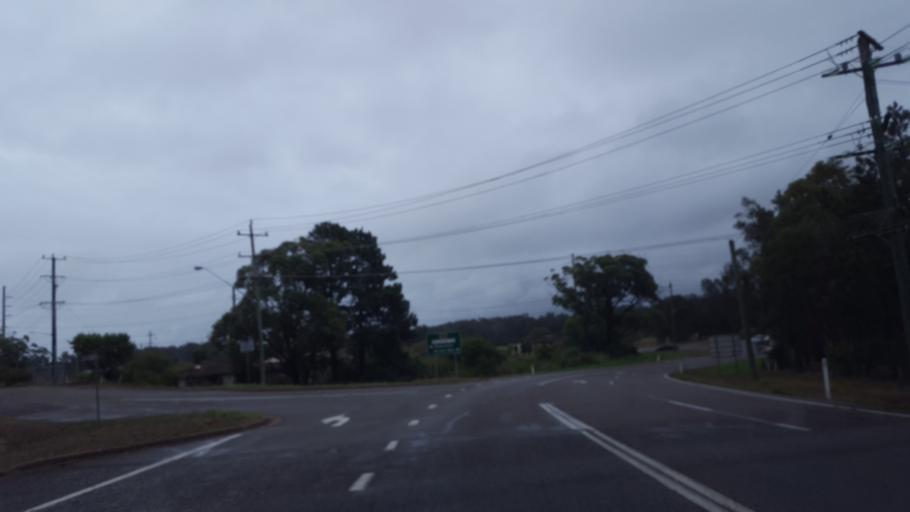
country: AU
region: New South Wales
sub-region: Port Stephens Shire
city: Anna Bay
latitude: -32.7704
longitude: 152.0749
